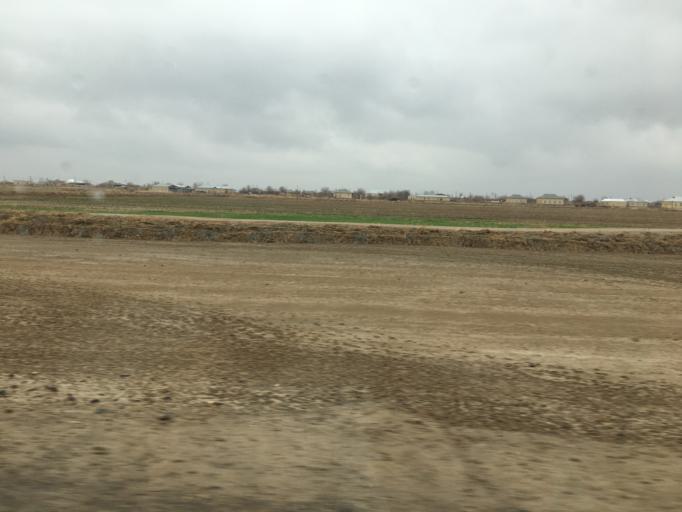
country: TM
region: Mary
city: Yoloeten
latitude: 37.4011
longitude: 62.1762
